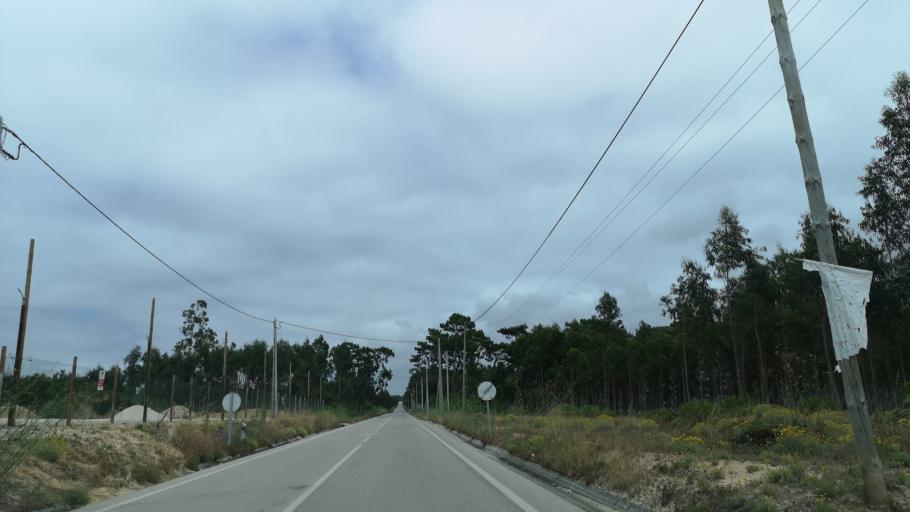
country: PT
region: Leiria
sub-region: Nazare
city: Nazare
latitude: 39.5209
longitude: -9.1183
